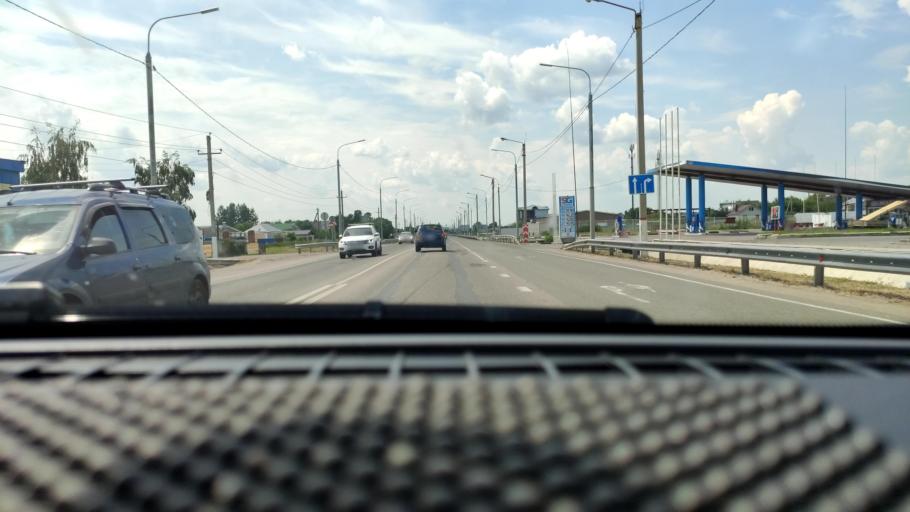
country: RU
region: Voronezj
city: Somovo
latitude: 51.6928
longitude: 39.3743
